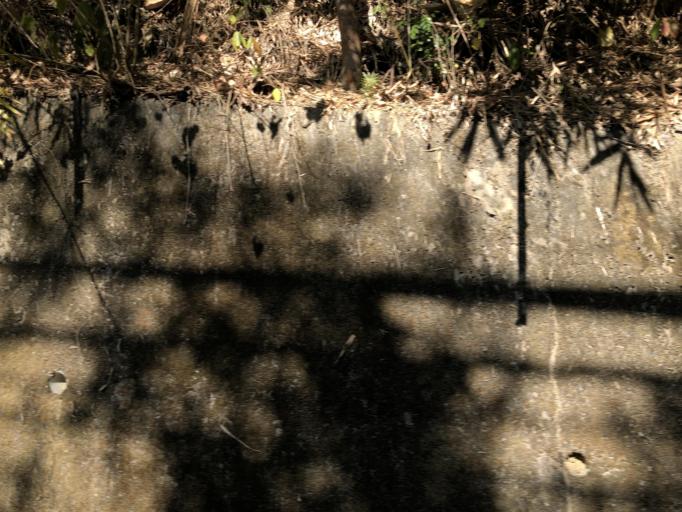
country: TW
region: Taiwan
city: Yujing
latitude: 23.0255
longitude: 120.3880
